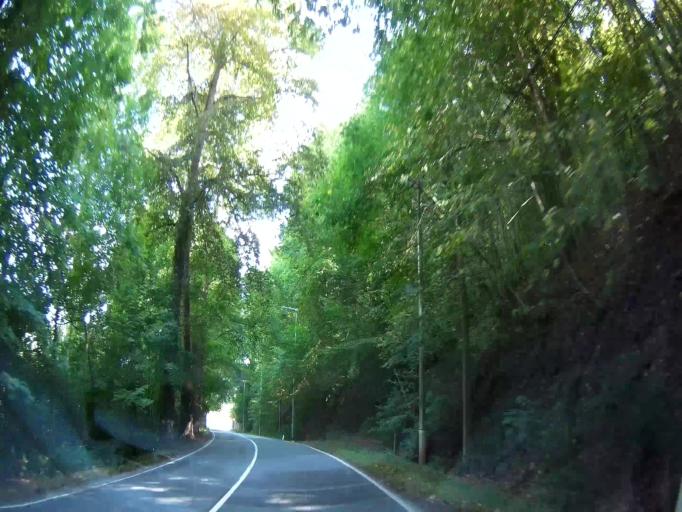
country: BE
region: Wallonia
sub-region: Province de Namur
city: Yvoir
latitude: 50.3375
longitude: 4.8632
